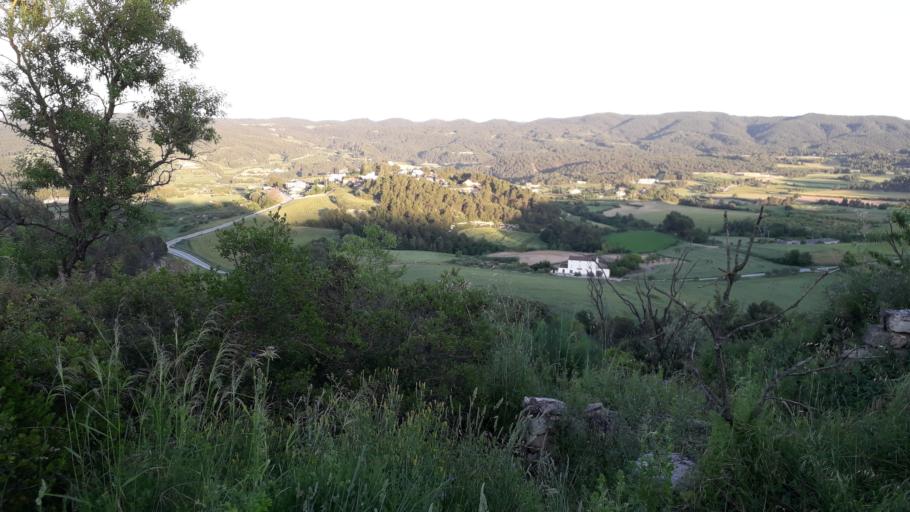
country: ES
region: Catalonia
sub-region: Provincia de Barcelona
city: Sant Marti de Tous
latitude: 41.5682
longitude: 1.5100
